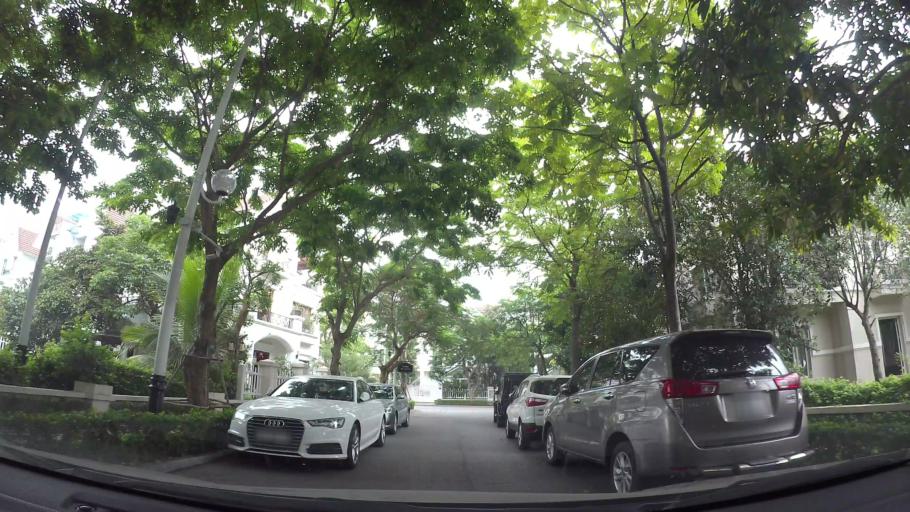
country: VN
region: Ha Noi
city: Trau Quy
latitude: 21.0451
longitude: 105.9147
